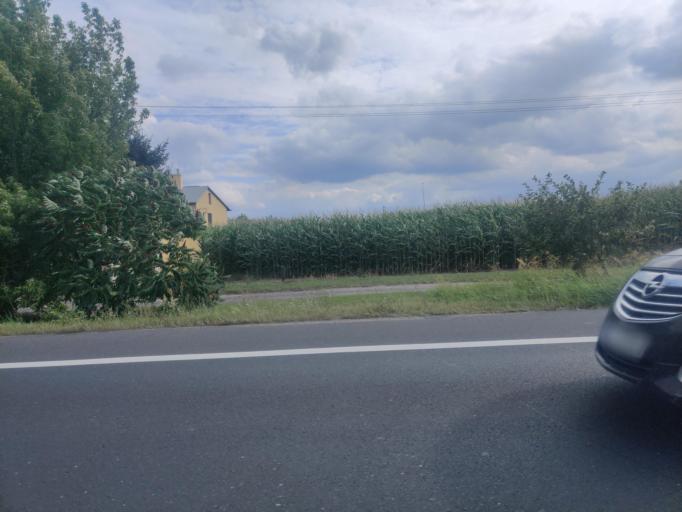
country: PL
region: Greater Poland Voivodeship
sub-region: Powiat koninski
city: Stare Miasto
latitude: 52.1892
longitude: 18.2458
